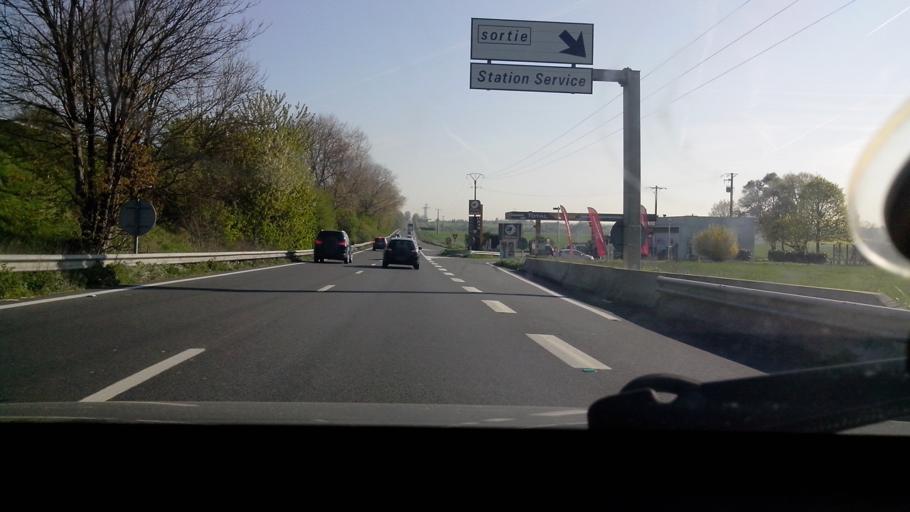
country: FR
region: Ile-de-France
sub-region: Departement de l'Essonne
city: Saclay
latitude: 48.7352
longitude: 2.1727
